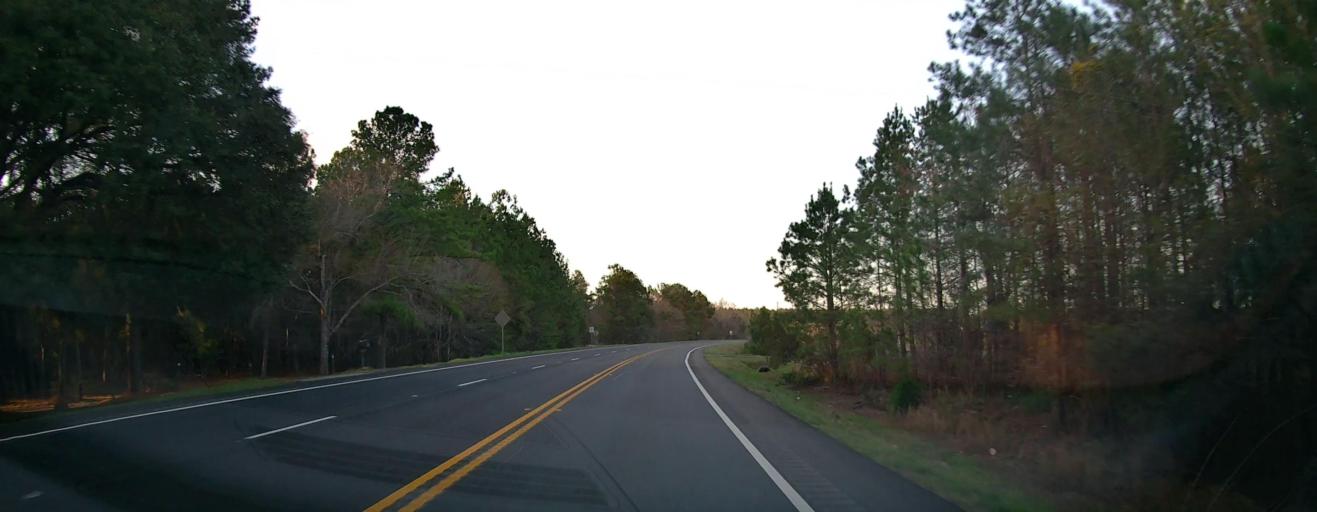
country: US
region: Georgia
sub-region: Bryan County
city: Pembroke
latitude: 32.1347
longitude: -81.5364
